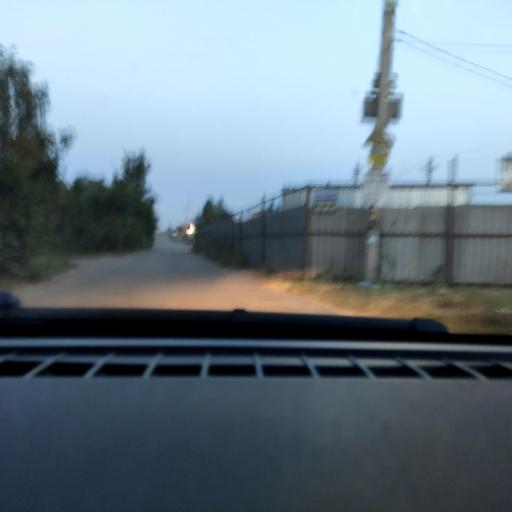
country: RU
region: Voronezj
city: Somovo
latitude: 51.6795
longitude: 39.3180
